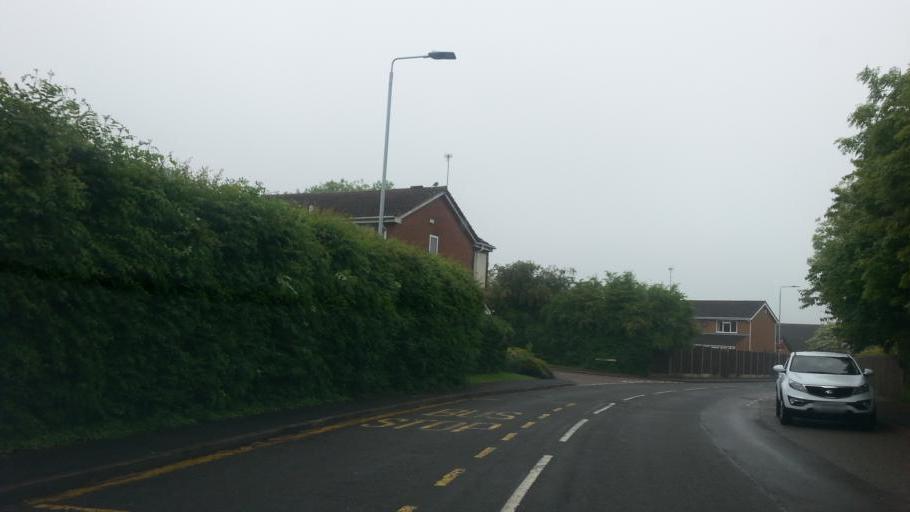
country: GB
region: England
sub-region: Leicestershire
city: Oadby
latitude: 52.5914
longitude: -1.0593
